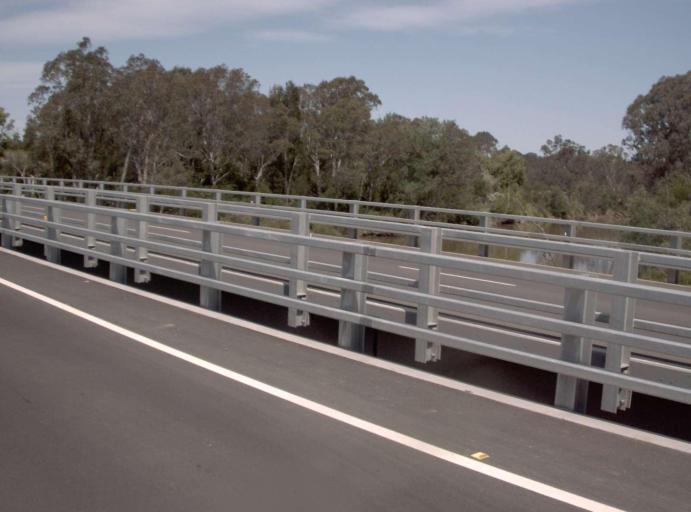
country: AU
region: Victoria
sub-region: Wellington
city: Sale
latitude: -38.1127
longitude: 147.0484
